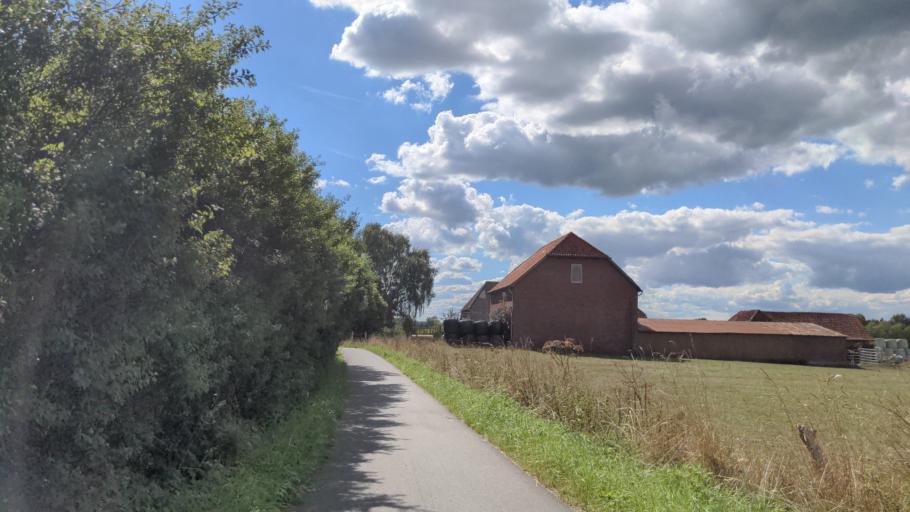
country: DE
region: Schleswig-Holstein
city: Kasseedorf
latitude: 54.1699
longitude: 10.7272
